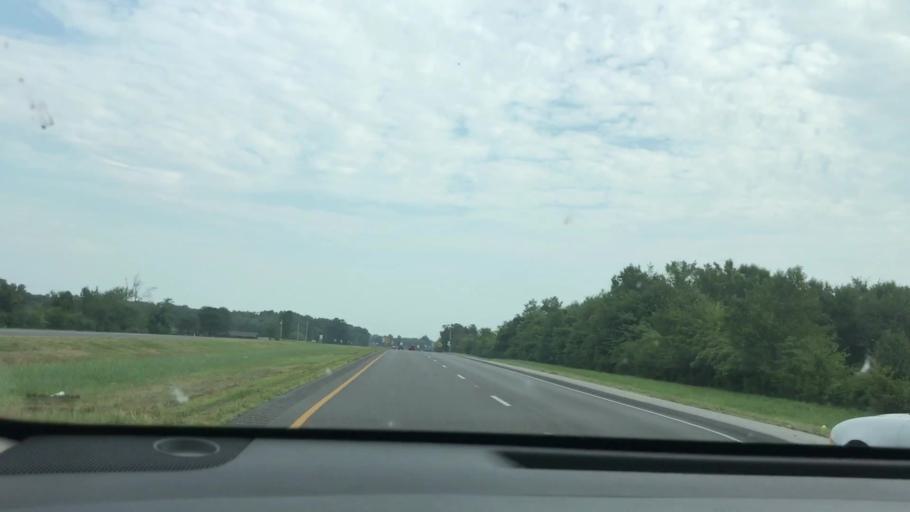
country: US
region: Kentucky
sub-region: Calloway County
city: Murray
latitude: 36.6940
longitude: -88.3031
